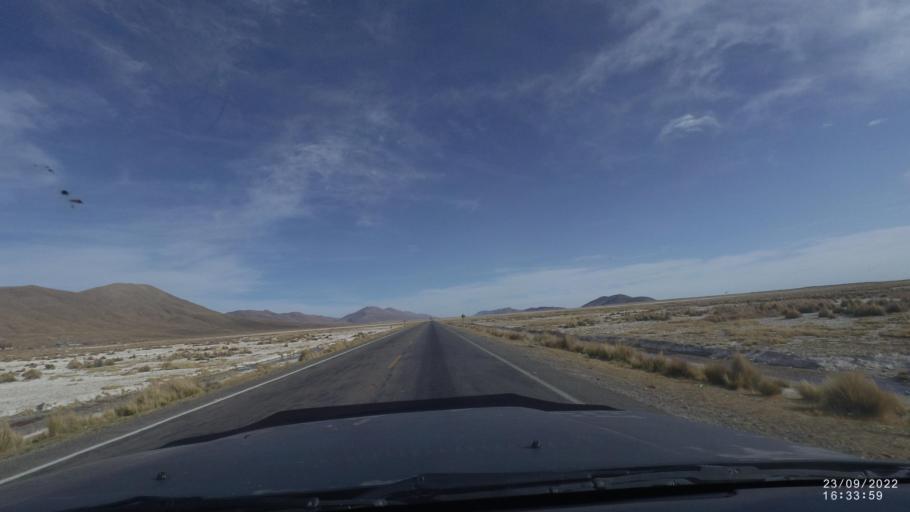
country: BO
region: Oruro
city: Machacamarca
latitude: -18.1822
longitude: -67.0158
